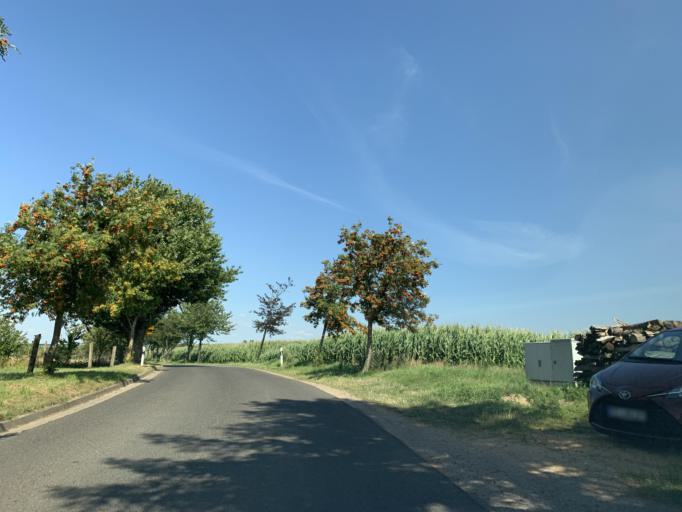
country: DE
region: Mecklenburg-Vorpommern
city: Loitz
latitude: 53.3401
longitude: 13.3882
